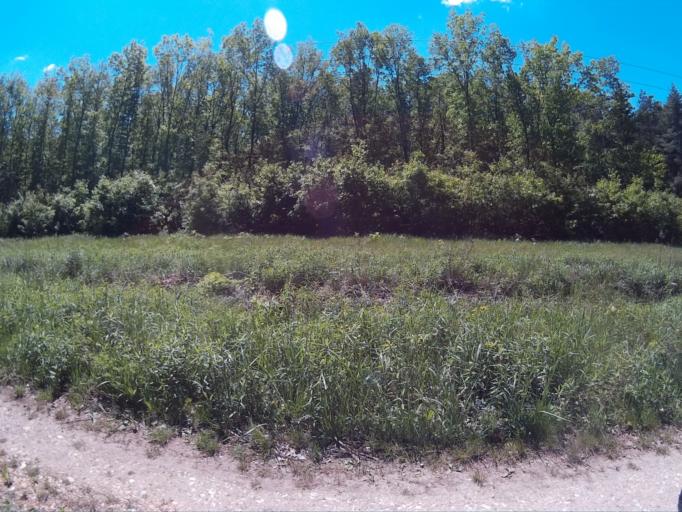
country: HU
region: Vas
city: Kormend
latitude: 46.9714
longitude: 16.5832
